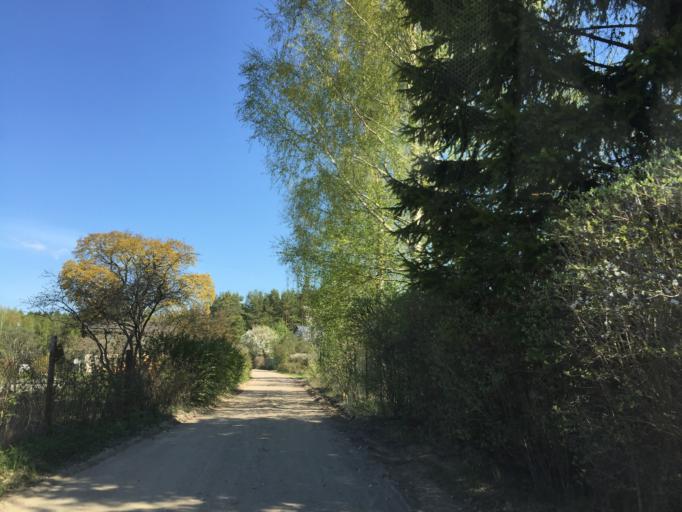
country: LV
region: Saulkrastu
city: Saulkrasti
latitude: 57.3123
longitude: 24.4330
